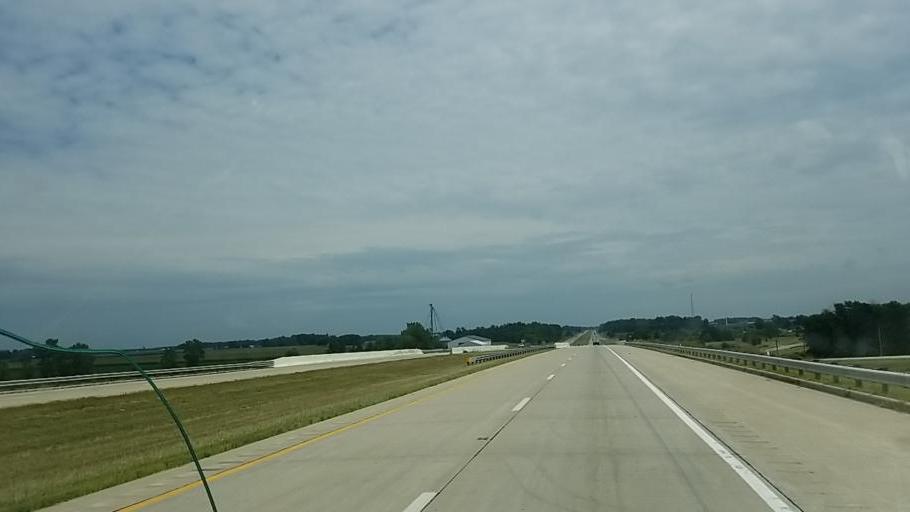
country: US
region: Ohio
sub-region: Crawford County
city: Bucyrus
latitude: 40.8266
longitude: -83.0434
